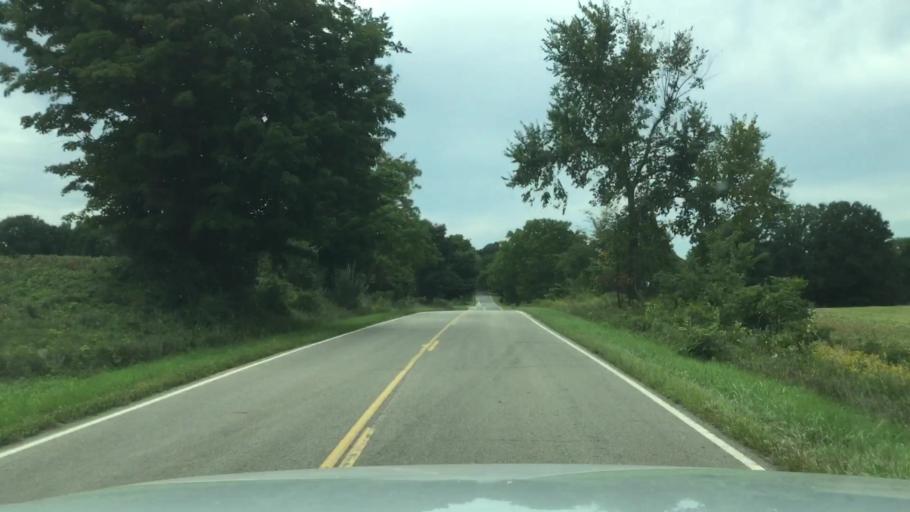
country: US
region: Michigan
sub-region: Shiawassee County
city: Corunna
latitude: 42.9361
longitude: -84.1023
